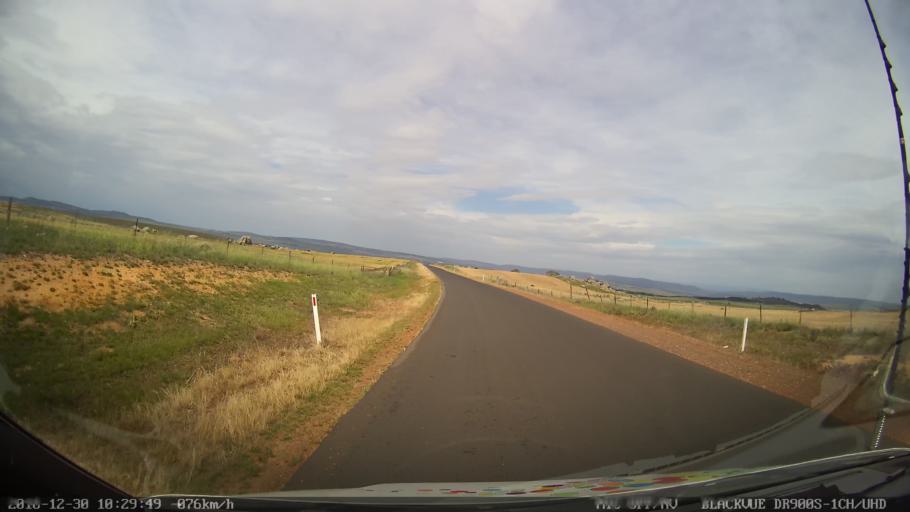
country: AU
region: New South Wales
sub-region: Snowy River
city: Berridale
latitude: -36.5014
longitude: 148.9038
